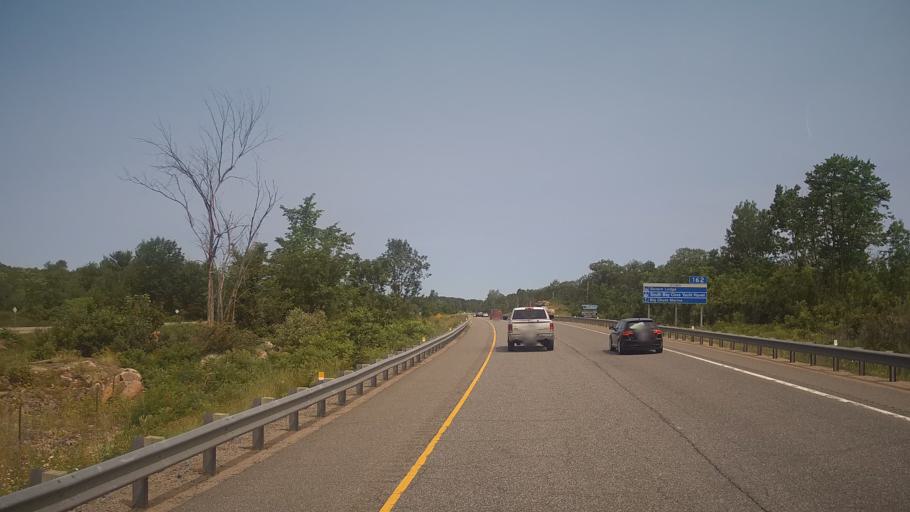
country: CA
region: Ontario
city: Midland
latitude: 44.8290
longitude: -79.7369
